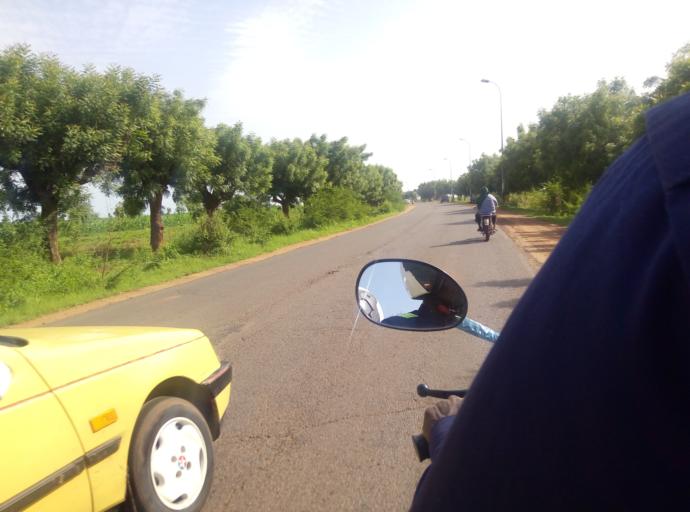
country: ML
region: Bamako
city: Bamako
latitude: 12.5539
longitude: -7.9470
